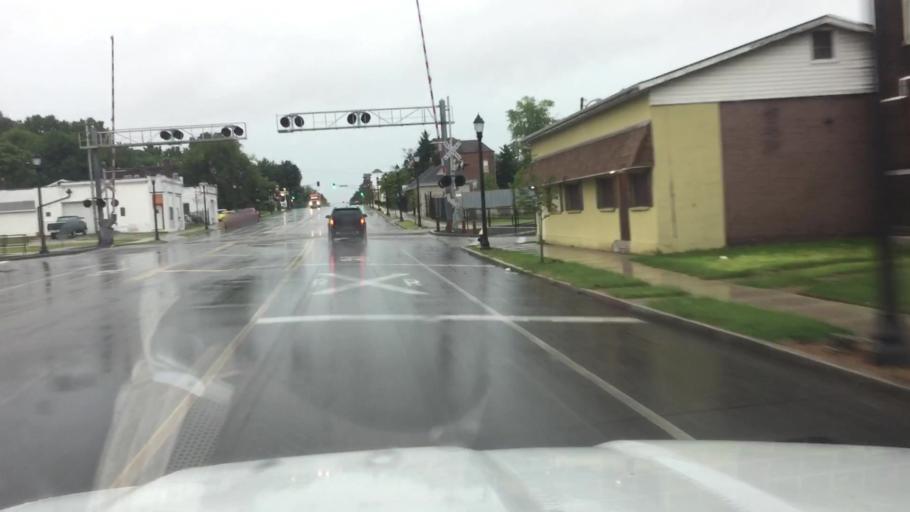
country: US
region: Missouri
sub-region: Saint Louis County
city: Lemay
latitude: 38.5449
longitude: -90.2609
